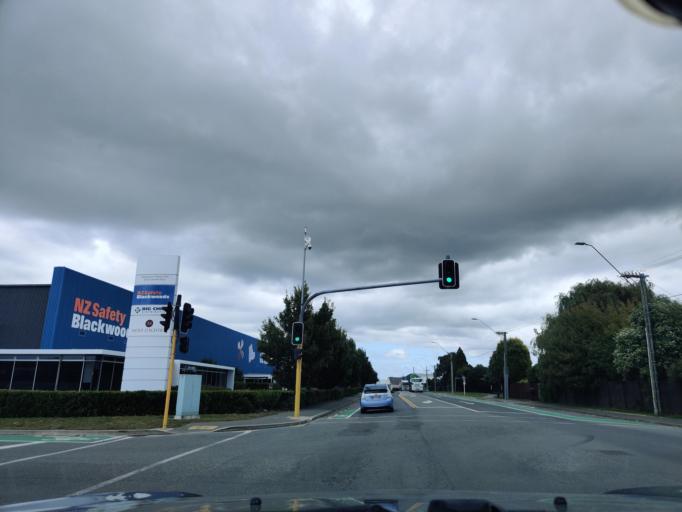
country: NZ
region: Canterbury
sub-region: Selwyn District
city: Prebbleton
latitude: -43.5479
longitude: 172.5206
